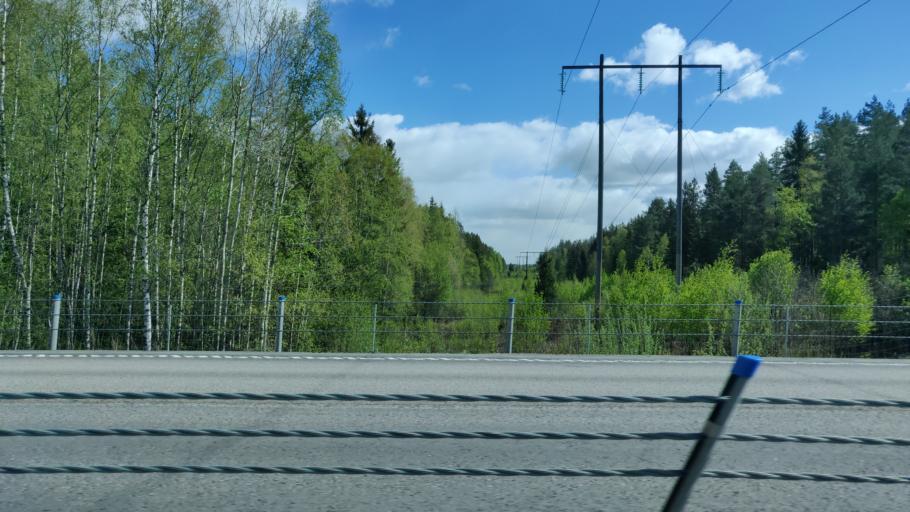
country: SE
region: Vaermland
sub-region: Karlstads Kommun
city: Karlstad
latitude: 59.4286
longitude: 13.5366
